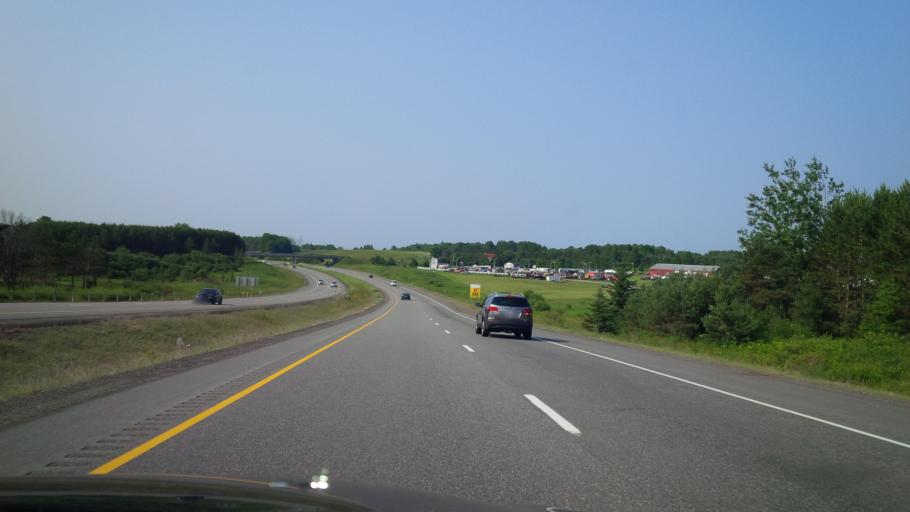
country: CA
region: Ontario
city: Bracebridge
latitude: 45.0401
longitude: -79.2901
